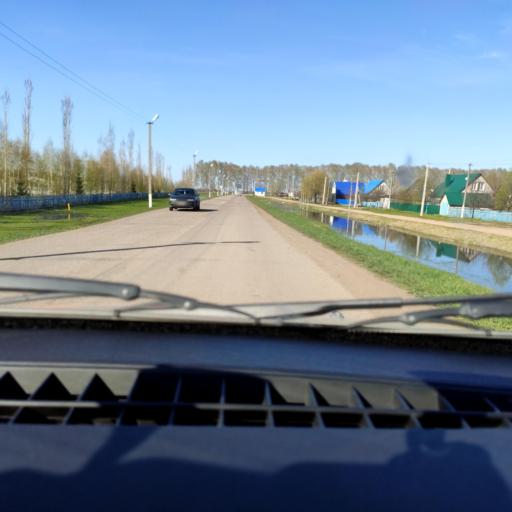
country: RU
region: Bashkortostan
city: Kabakovo
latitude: 54.6026
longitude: 56.1849
